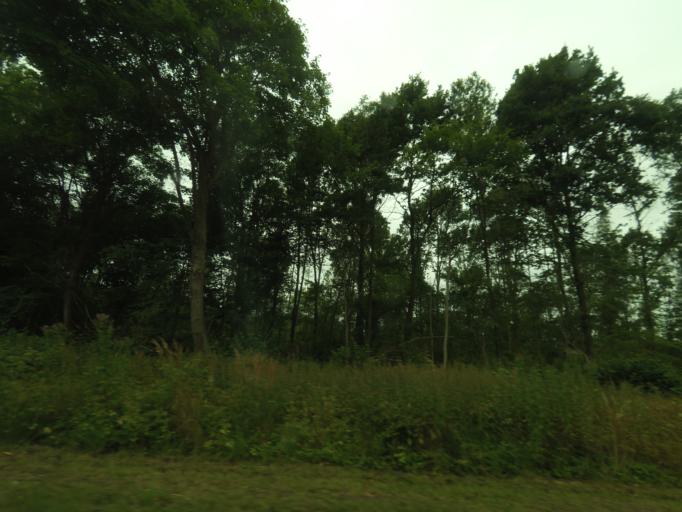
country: DK
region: South Denmark
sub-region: Odense Kommune
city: Stige
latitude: 55.4354
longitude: 10.3756
